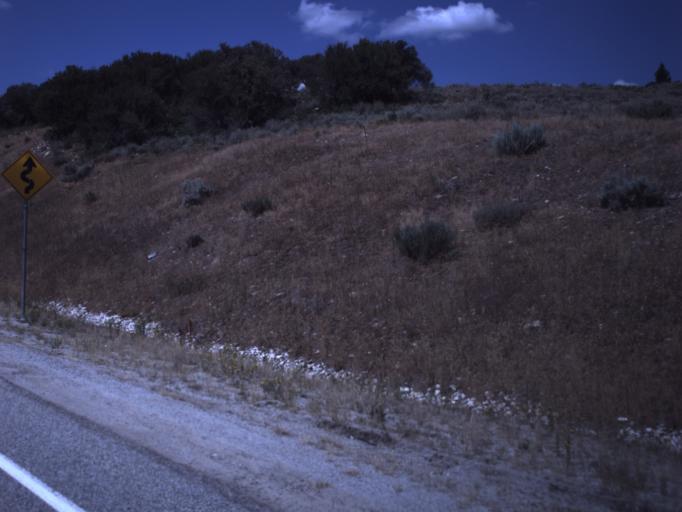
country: US
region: Idaho
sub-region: Bear Lake County
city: Paris
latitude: 41.9218
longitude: -111.4606
